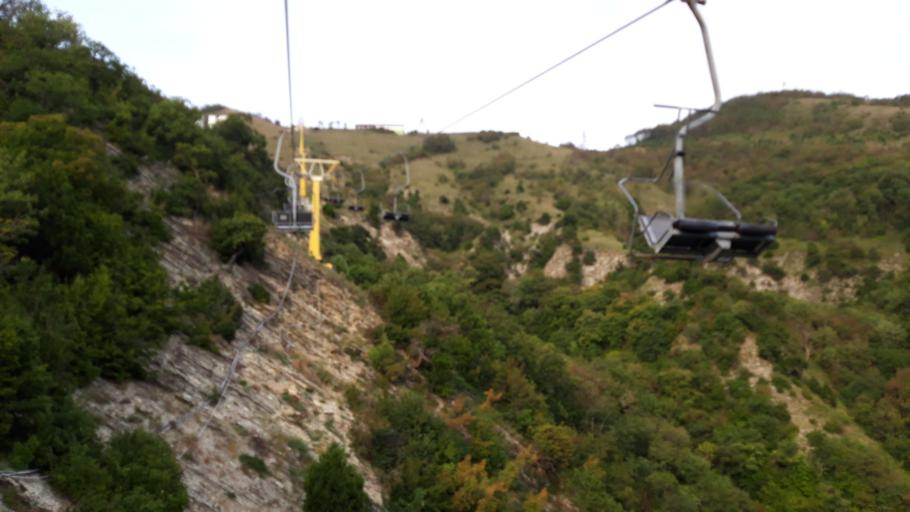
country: RU
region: Krasnodarskiy
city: Gelendzhik
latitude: 44.5814
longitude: 38.0973
